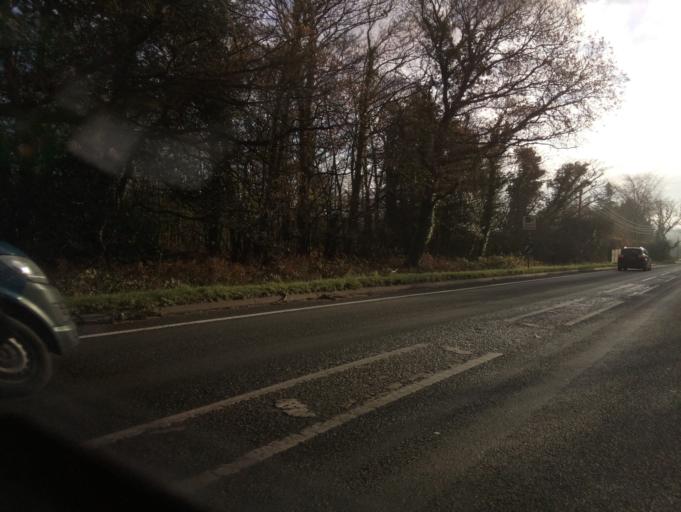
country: GB
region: England
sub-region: City and Borough of Birmingham
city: Sutton Coldfield
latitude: 52.5774
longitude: -1.7721
